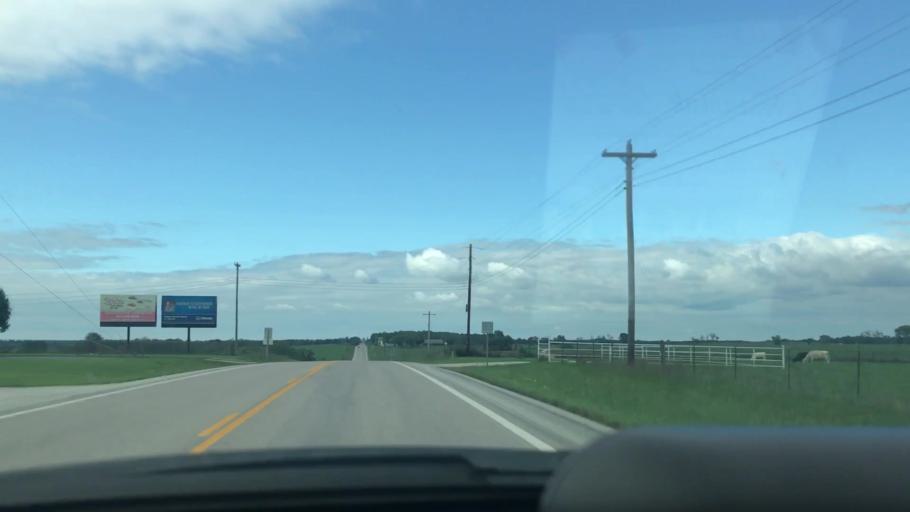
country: US
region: Missouri
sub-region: Hickory County
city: Hermitage
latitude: 37.9473
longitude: -93.2077
